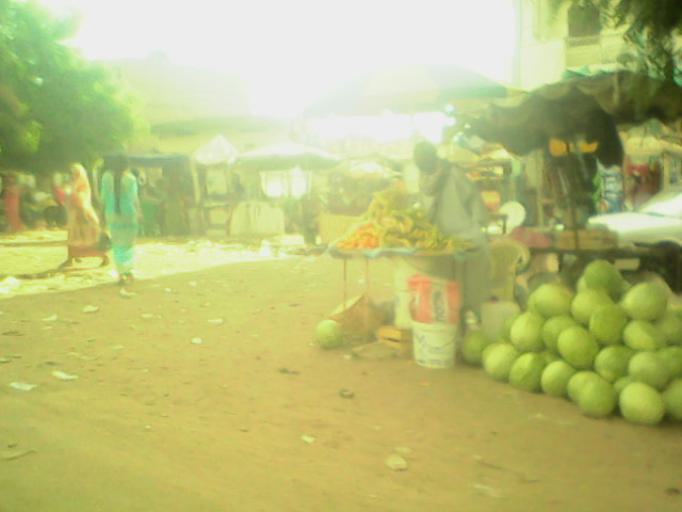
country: SN
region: Diourbel
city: Touba
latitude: 14.8759
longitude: -15.9007
